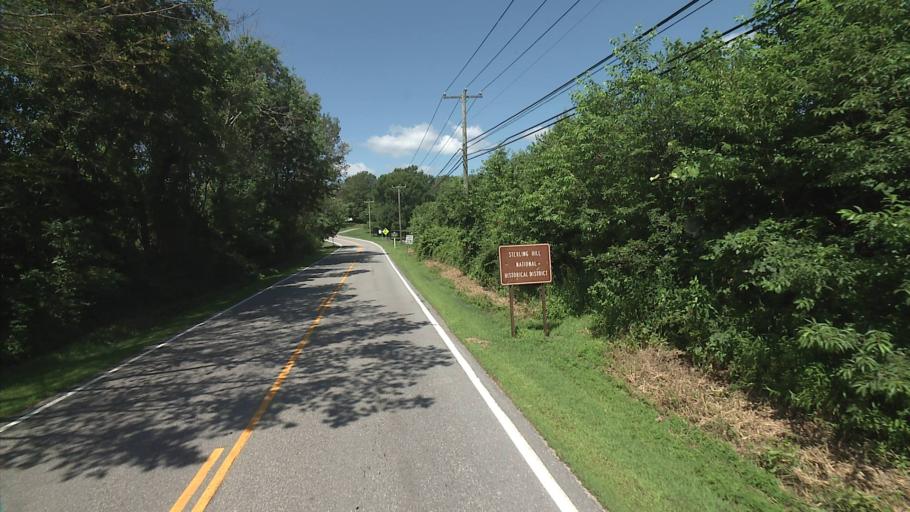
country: US
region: Connecticut
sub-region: Windham County
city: Moosup
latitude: 41.6912
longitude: -71.8439
